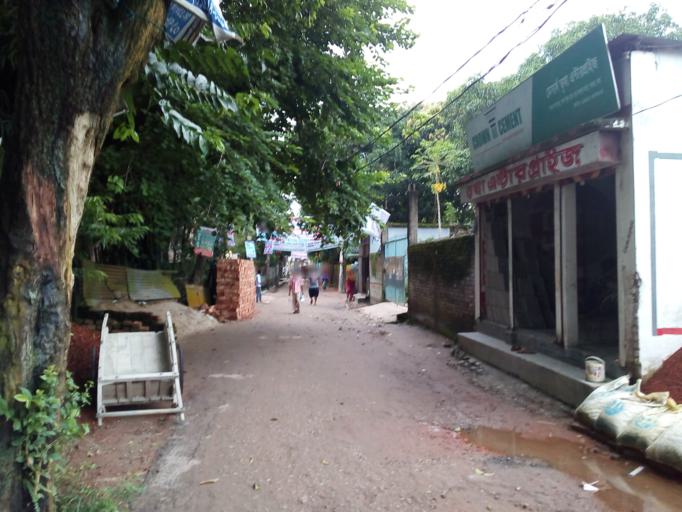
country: BD
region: Dhaka
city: Tungi
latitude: 23.8419
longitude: 90.2501
